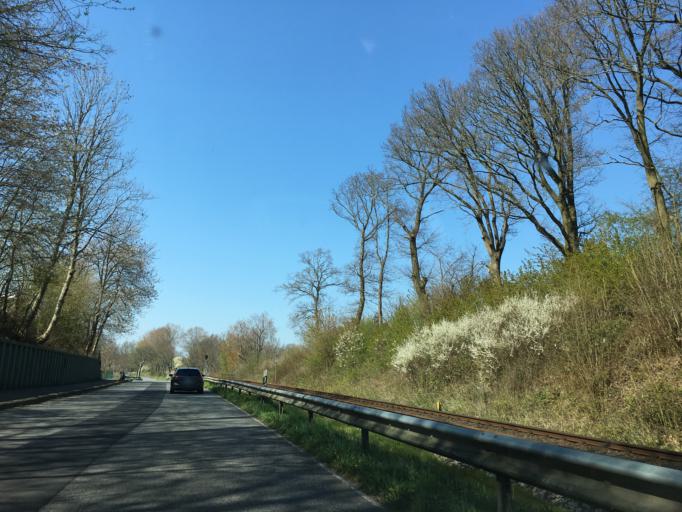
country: DE
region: Schleswig-Holstein
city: Dollrottfeld
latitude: 54.5880
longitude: 9.8146
